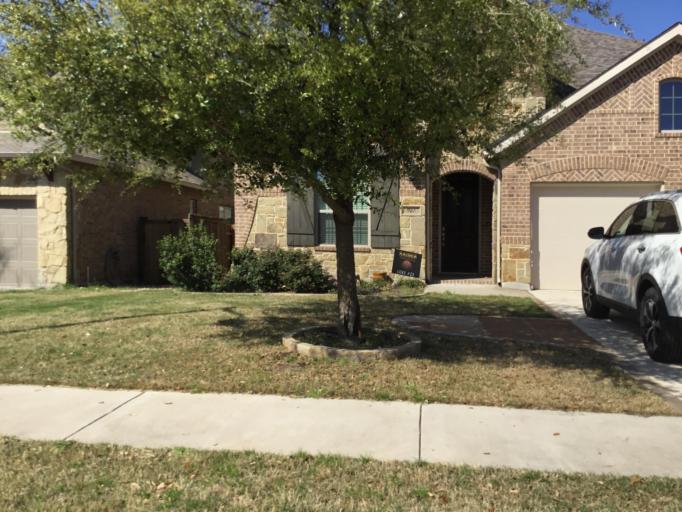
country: US
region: Texas
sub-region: Williamson County
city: Brushy Creek
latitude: 30.5744
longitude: -97.7690
